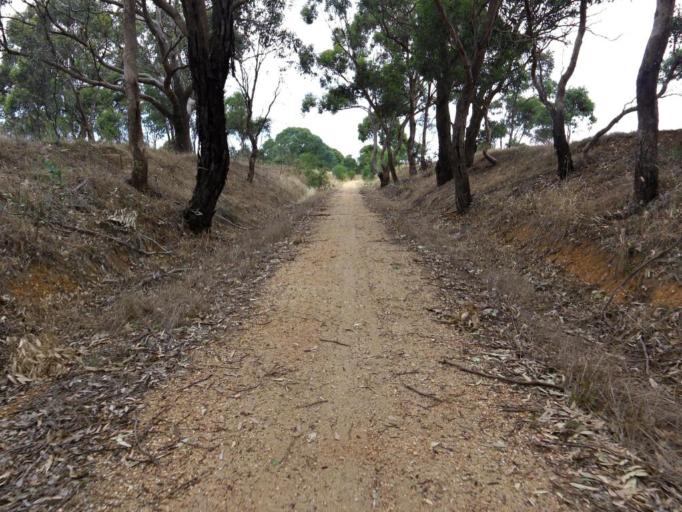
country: AU
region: Victoria
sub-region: Greater Bendigo
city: Kennington
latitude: -36.8568
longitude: 144.6201
